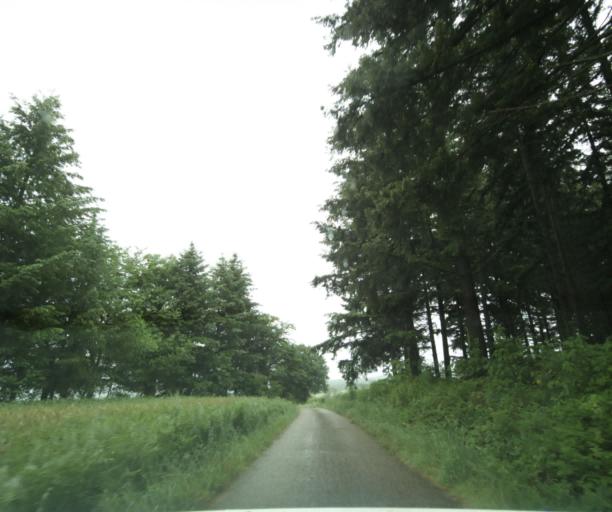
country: FR
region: Bourgogne
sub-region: Departement de Saone-et-Loire
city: Charolles
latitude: 46.4454
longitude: 4.3966
